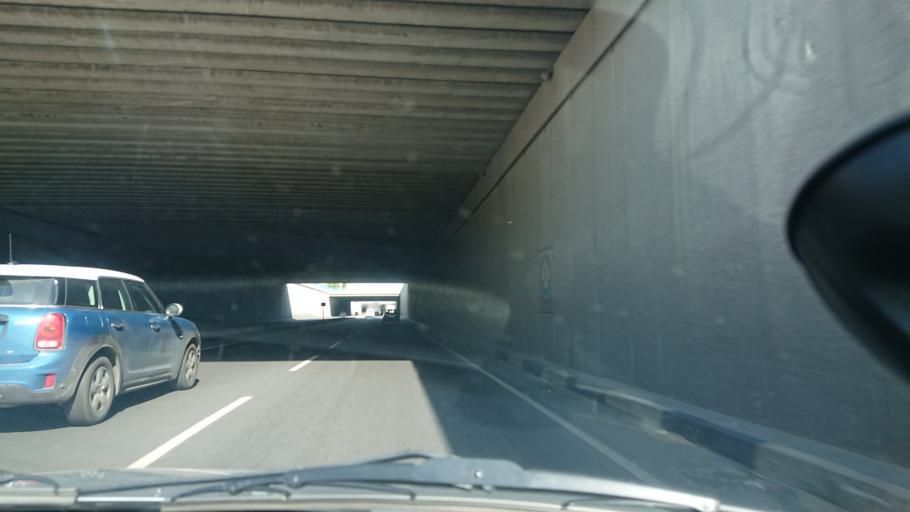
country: TR
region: Manisa
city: Turgutlu
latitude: 38.4901
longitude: 27.7032
